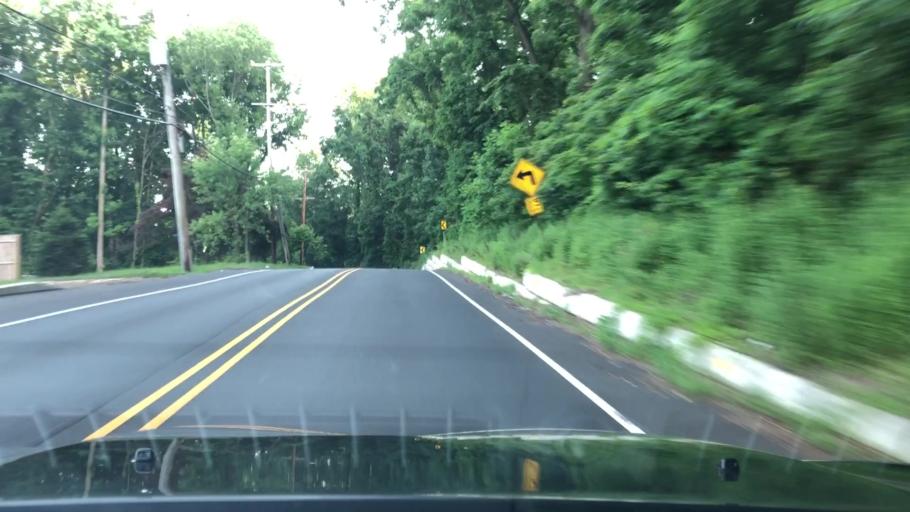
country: US
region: Pennsylvania
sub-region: Bucks County
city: Langhorne Manor
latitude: 40.1716
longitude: -74.9012
